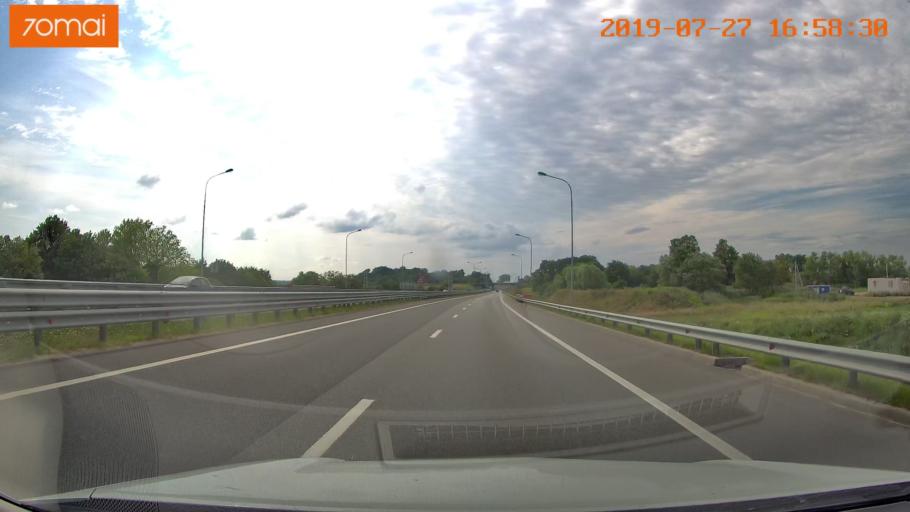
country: RU
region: Kaliningrad
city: Bol'shoe Isakovo
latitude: 54.7012
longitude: 20.6790
